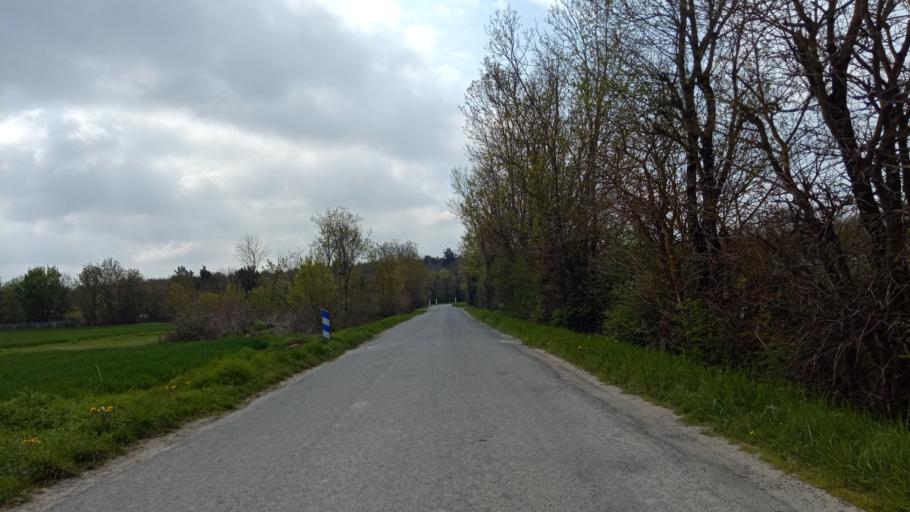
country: FR
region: Poitou-Charentes
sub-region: Departement de la Charente-Maritime
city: Verines
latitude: 46.1494
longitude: -0.9361
